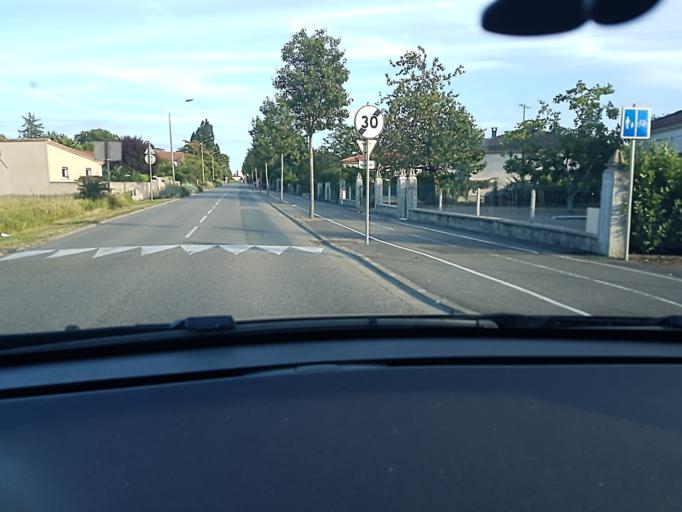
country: FR
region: Aquitaine
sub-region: Departement du Lot-et-Garonne
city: Nerac
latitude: 44.1297
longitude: 0.3489
